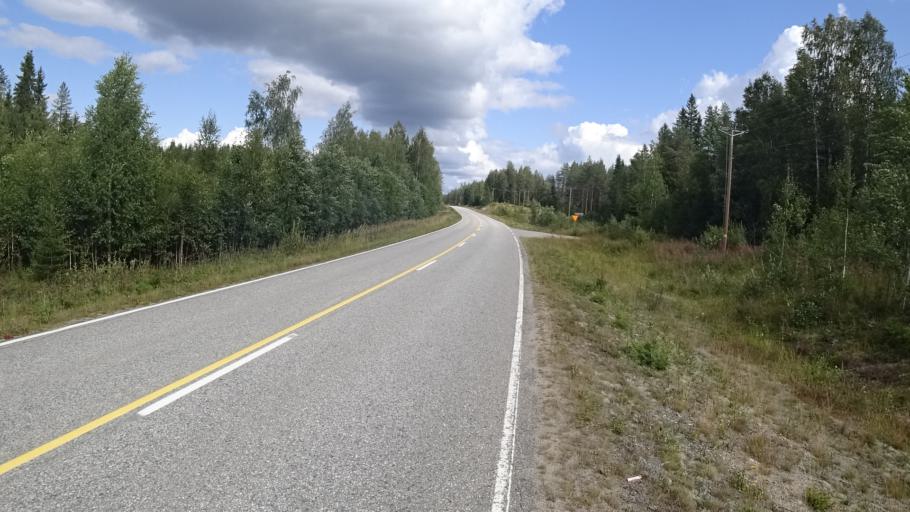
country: FI
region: North Karelia
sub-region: Joensuu
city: Ilomantsi
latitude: 62.6289
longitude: 31.2701
